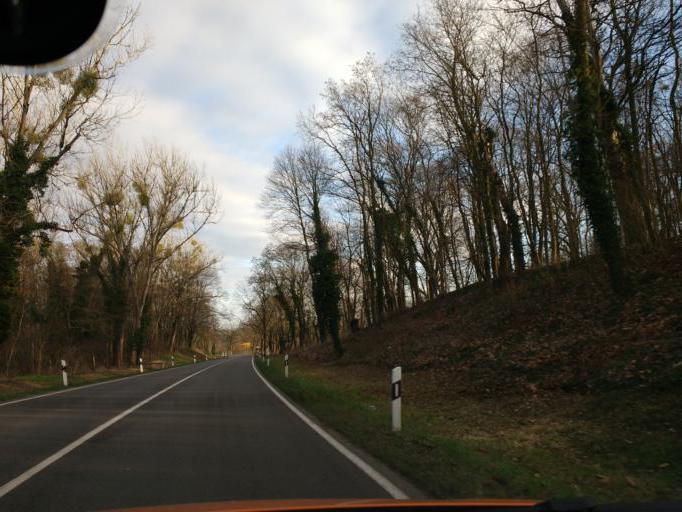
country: DE
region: Brandenburg
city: Wriezen
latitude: 52.7091
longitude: 14.1277
